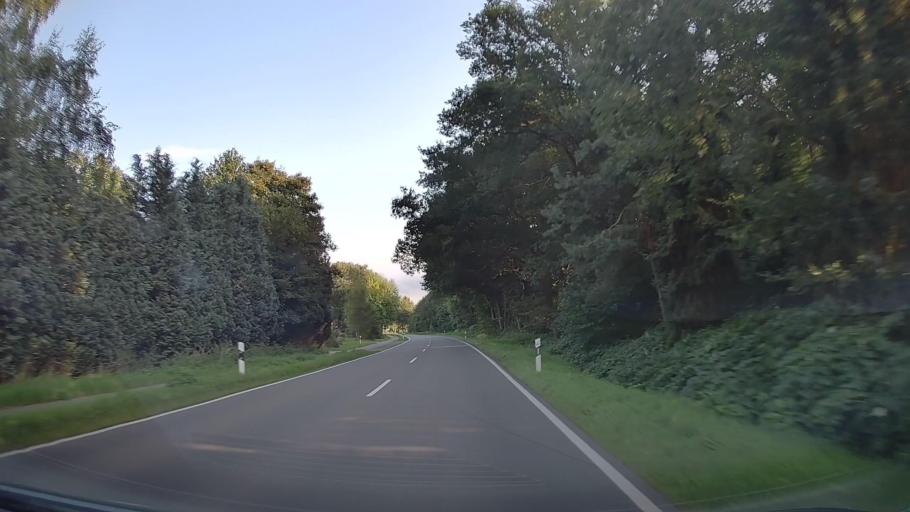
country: DE
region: Lower Saxony
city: Hilkenbrook
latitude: 53.0560
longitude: 7.7269
